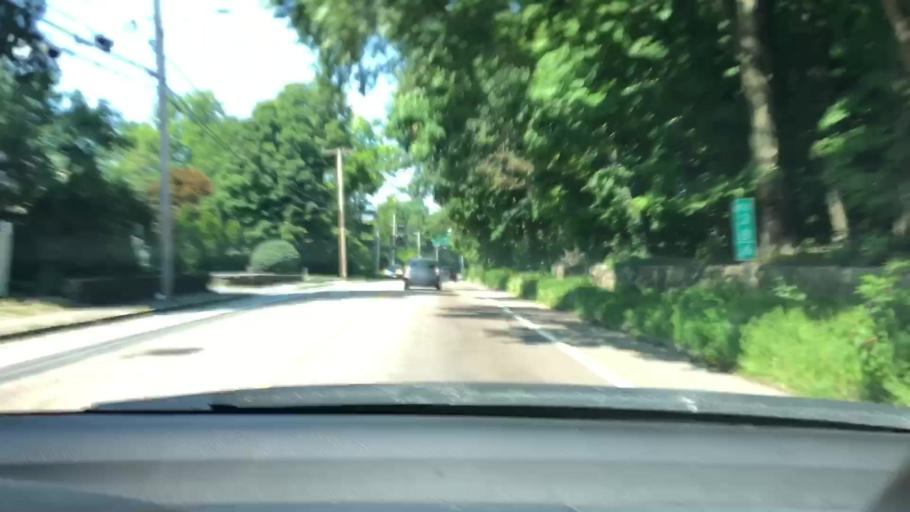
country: US
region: Massachusetts
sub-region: Norfolk County
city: Canton
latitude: 42.1956
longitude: -71.1189
